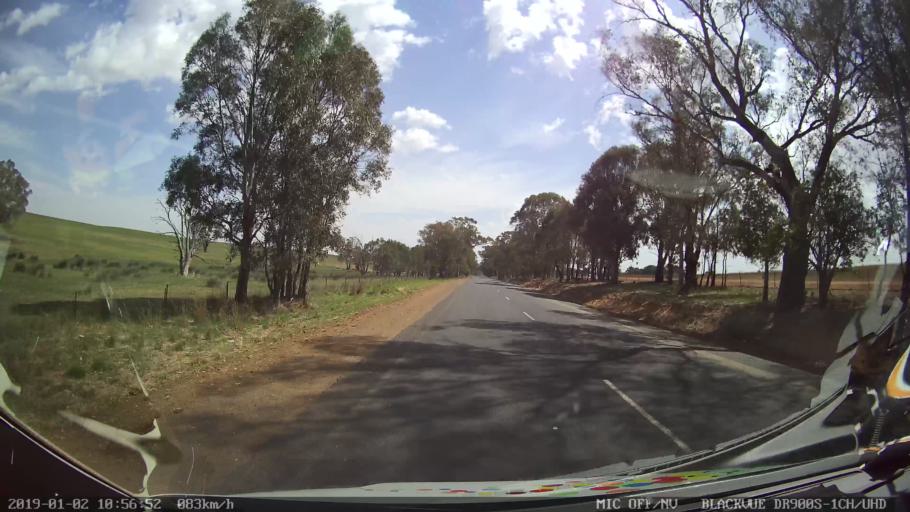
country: AU
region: New South Wales
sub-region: Cootamundra
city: Cootamundra
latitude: -34.6420
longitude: 148.2794
